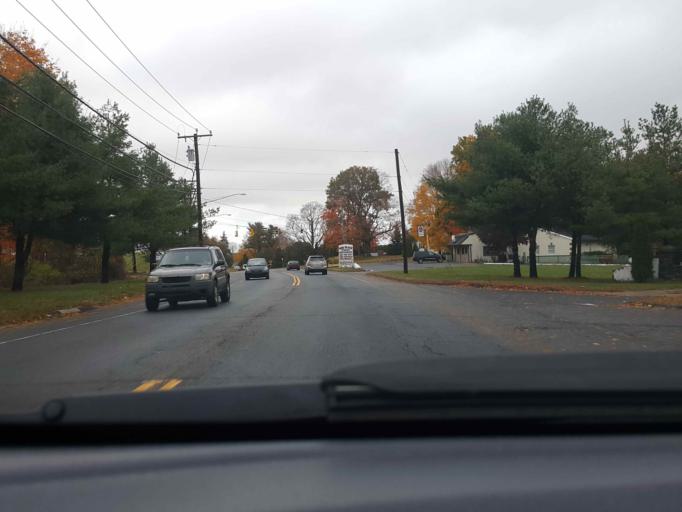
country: US
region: Connecticut
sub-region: Middlesex County
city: Durham
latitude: 41.5025
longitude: -72.6733
